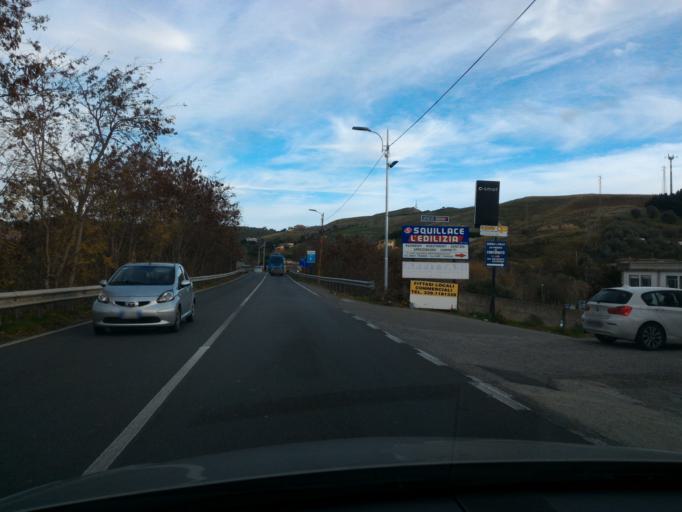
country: IT
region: Calabria
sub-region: Provincia di Catanzaro
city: Catanzaro
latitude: 38.8802
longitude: 16.6021
